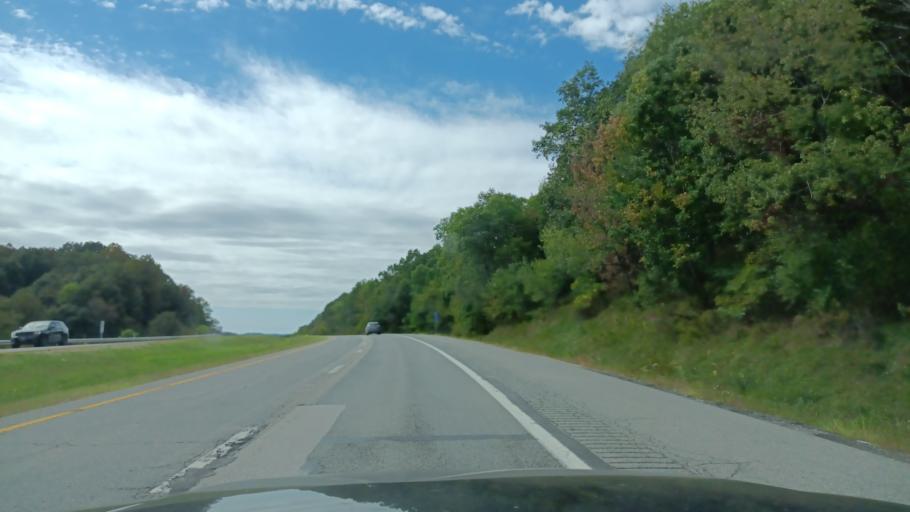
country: US
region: West Virginia
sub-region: Ritchie County
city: Harrisville
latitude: 39.2612
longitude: -81.1575
